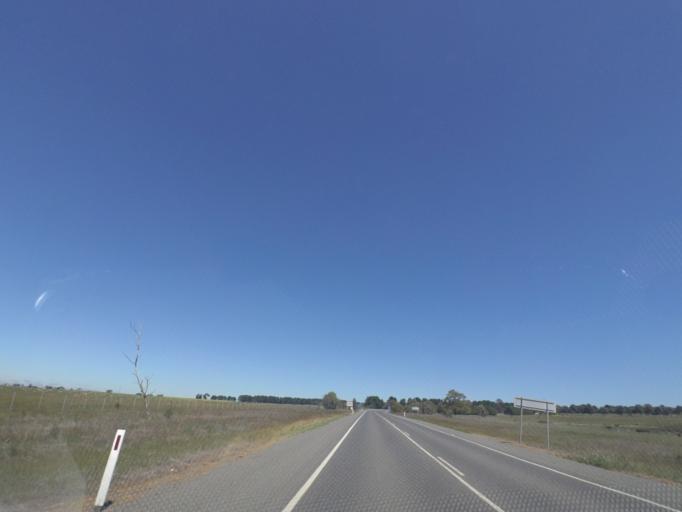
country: AU
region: Victoria
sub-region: Hume
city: Sunbury
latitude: -37.3093
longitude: 144.8543
